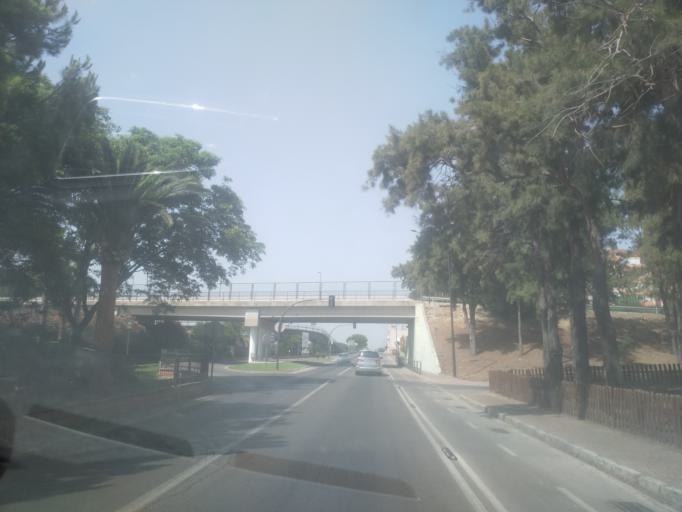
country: ES
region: Andalusia
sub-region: Provincia de Cadiz
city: San Fernando
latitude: 36.4630
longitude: -6.2091
